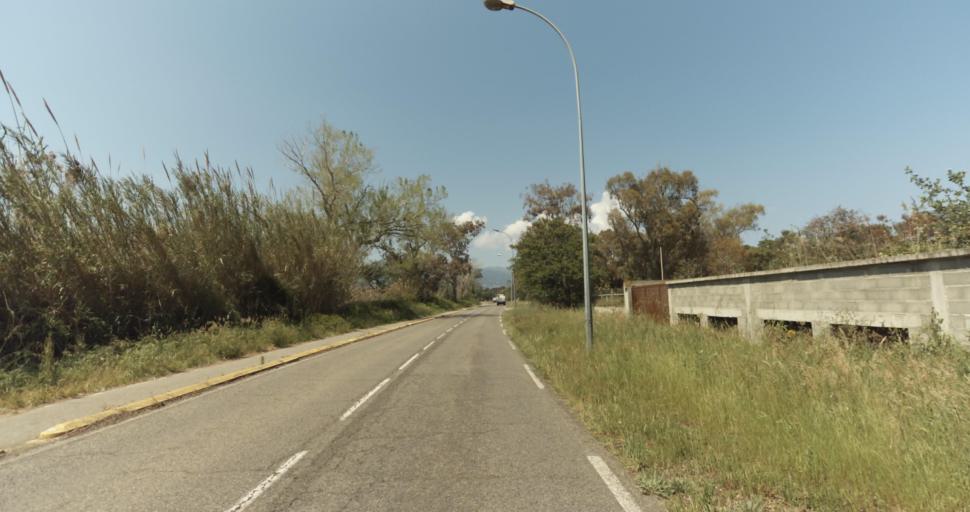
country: FR
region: Corsica
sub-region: Departement de la Haute-Corse
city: Biguglia
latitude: 42.6255
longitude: 9.4694
